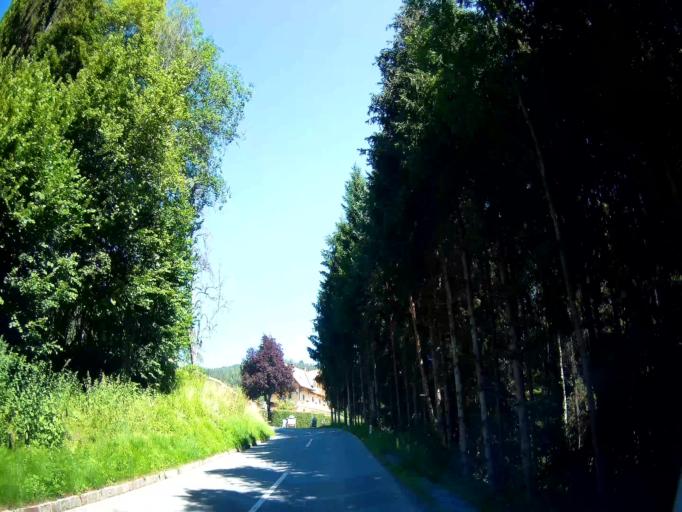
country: AT
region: Carinthia
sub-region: Politischer Bezirk Klagenfurt Land
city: Maria Worth
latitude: 46.6004
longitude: 14.1513
